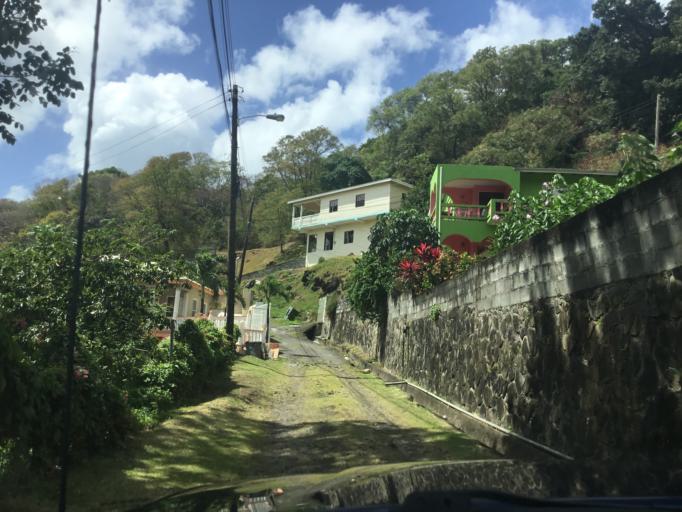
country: VC
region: Saint George
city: Kingstown Park
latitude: 13.1582
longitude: -61.2365
